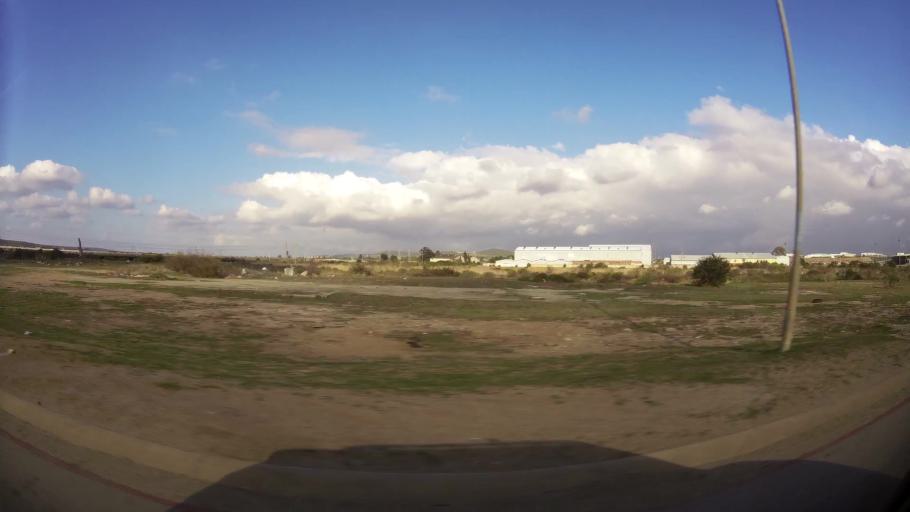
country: ZA
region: Eastern Cape
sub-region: Nelson Mandela Bay Metropolitan Municipality
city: Uitenhage
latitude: -33.7889
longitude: 25.4228
